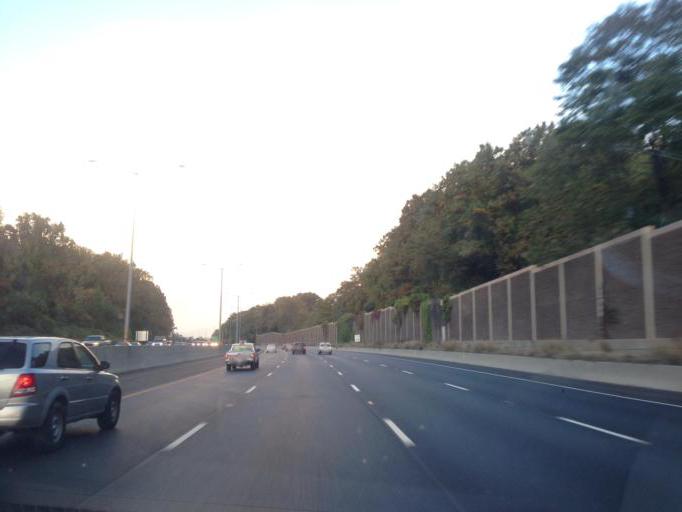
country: US
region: Maryland
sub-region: Baltimore County
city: Pikesville
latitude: 39.3951
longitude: -76.6989
